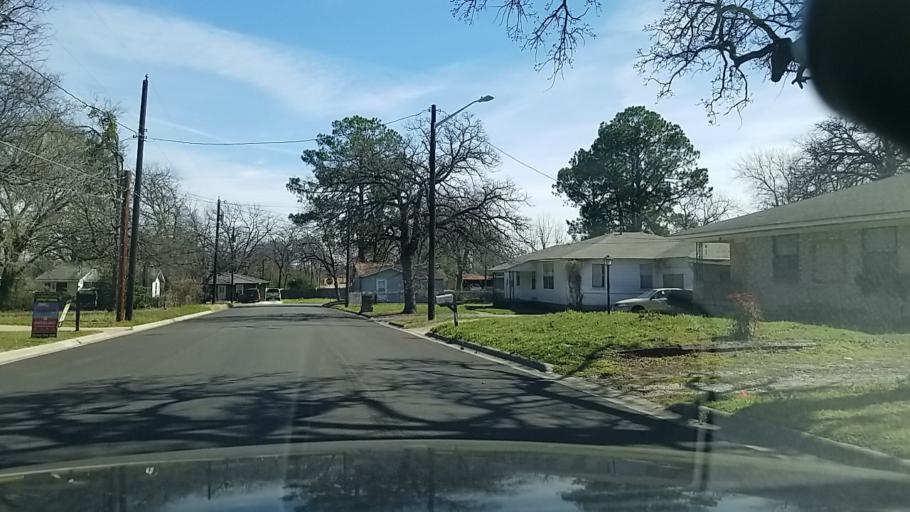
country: US
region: Texas
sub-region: Denton County
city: Denton
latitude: 33.2054
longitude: -97.1264
